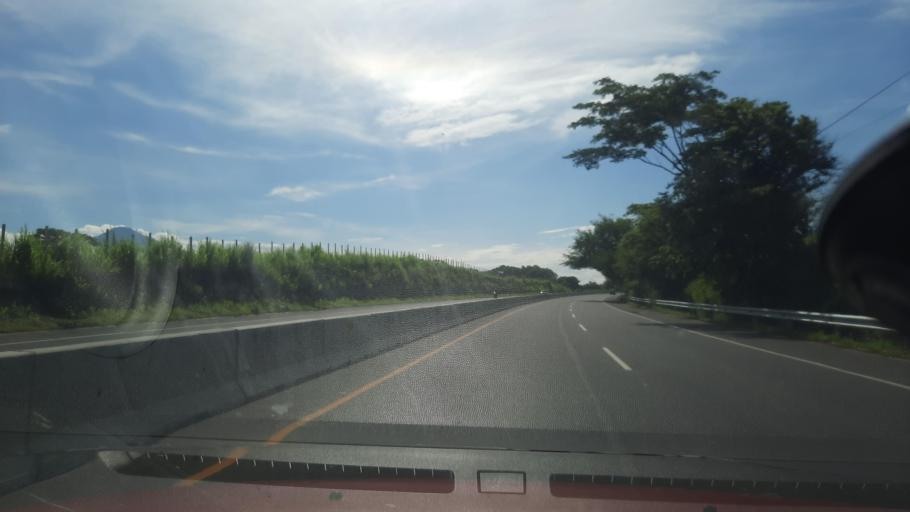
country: SV
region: La Paz
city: Santiago Nonualco
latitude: 13.4871
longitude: -88.9668
